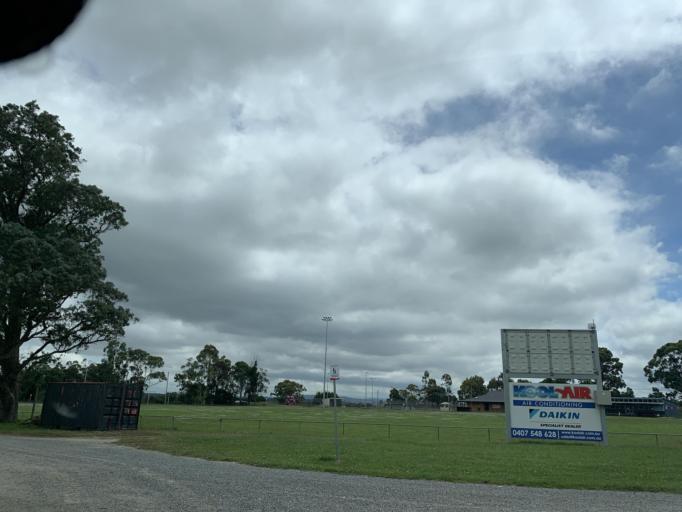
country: AU
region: Victoria
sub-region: Latrobe
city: Traralgon
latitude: -38.1504
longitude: 146.4809
